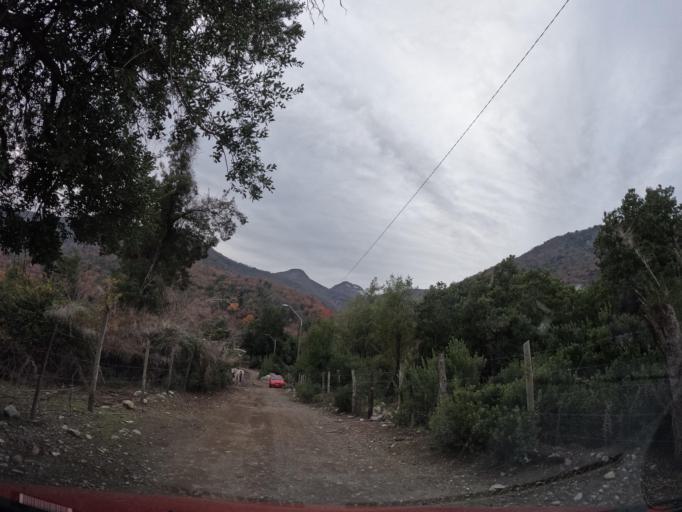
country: CL
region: Maule
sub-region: Provincia de Linares
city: Colbun
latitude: -35.7240
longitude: -71.0179
